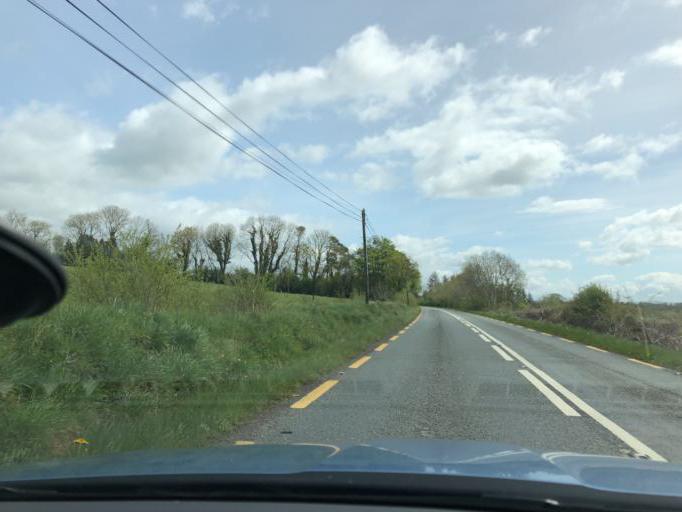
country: IE
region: Munster
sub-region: County Cork
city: Millstreet
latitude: 52.0845
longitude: -9.1819
